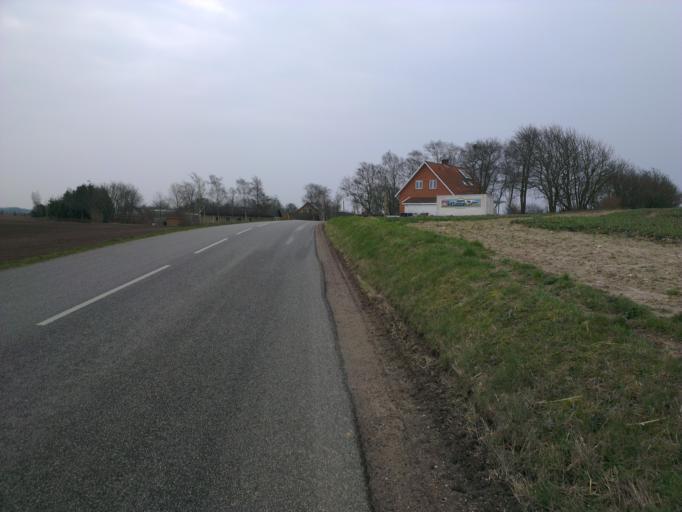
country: DK
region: Capital Region
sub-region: Frederikssund Kommune
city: Skibby
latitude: 55.7514
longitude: 11.9182
